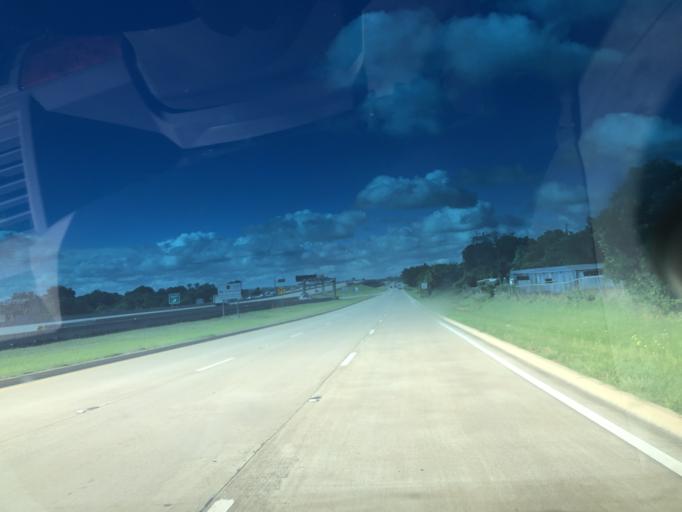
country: US
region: Texas
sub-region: Dallas County
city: Grand Prairie
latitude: 32.8086
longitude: -97.0190
